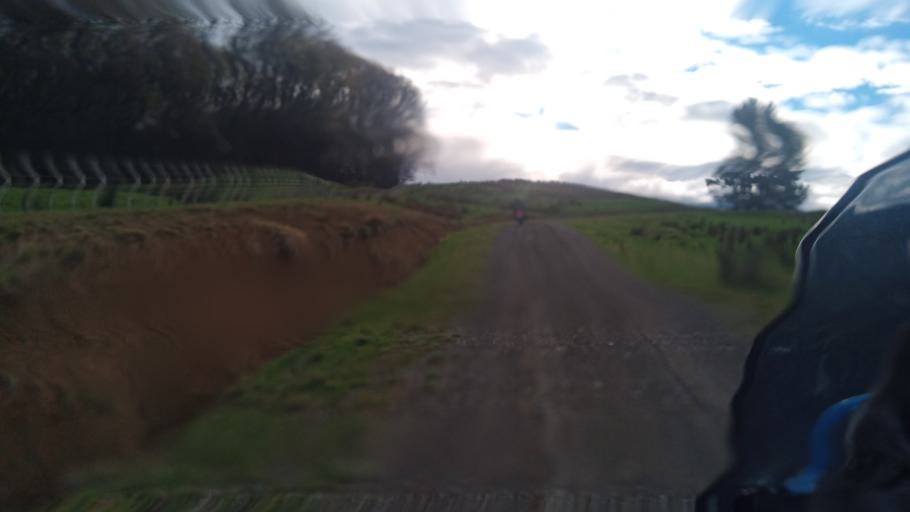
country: NZ
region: Gisborne
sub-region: Gisborne District
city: Gisborne
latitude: -38.3506
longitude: 177.9355
